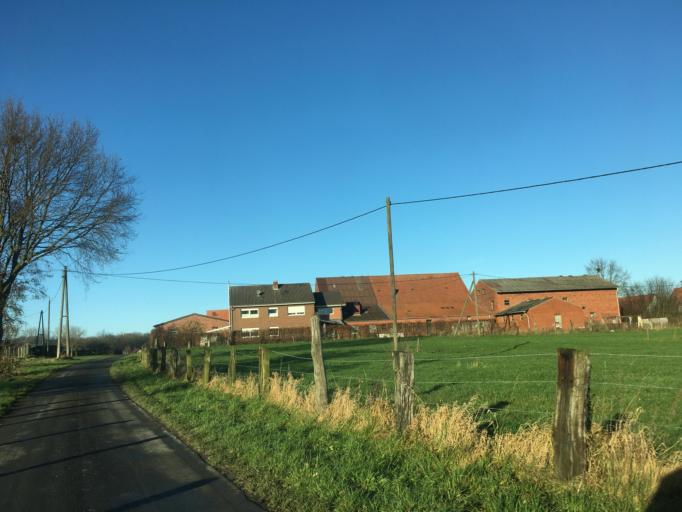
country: DE
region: North Rhine-Westphalia
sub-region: Regierungsbezirk Munster
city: Dulmen
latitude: 51.8628
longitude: 7.2983
